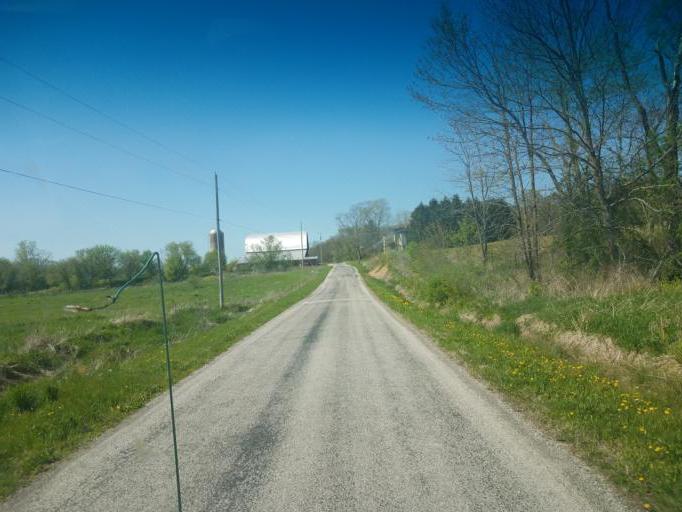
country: US
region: Ohio
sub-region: Medina County
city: Lodi
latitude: 40.9537
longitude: -82.0242
